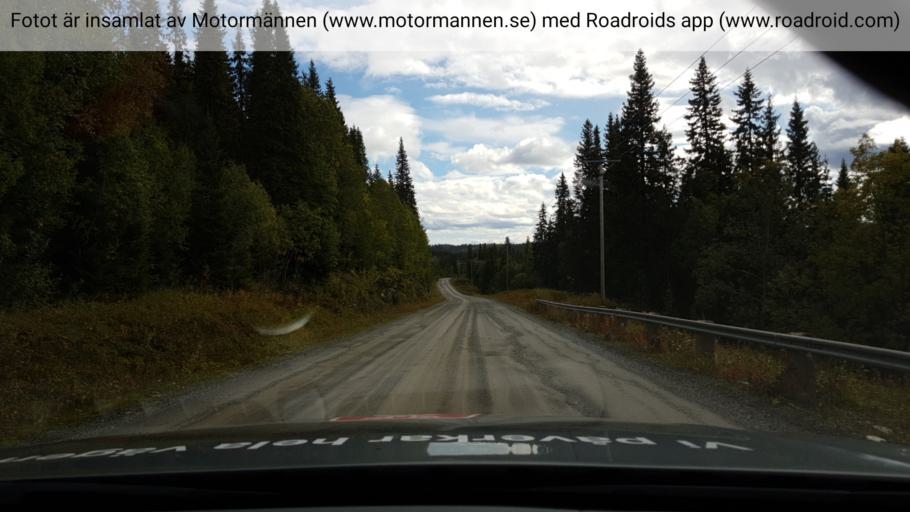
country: SE
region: Jaemtland
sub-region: Are Kommun
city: Are
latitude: 63.6961
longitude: 12.7893
